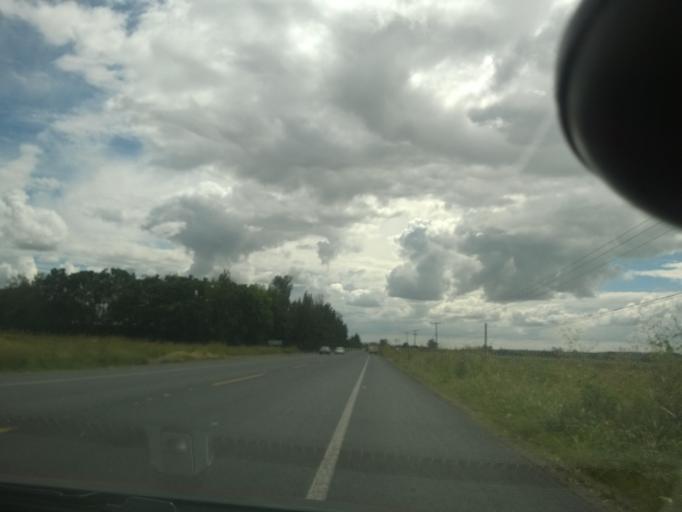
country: MX
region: Guanajuato
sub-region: Leon
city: El CERESO
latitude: 21.0082
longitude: -101.7012
